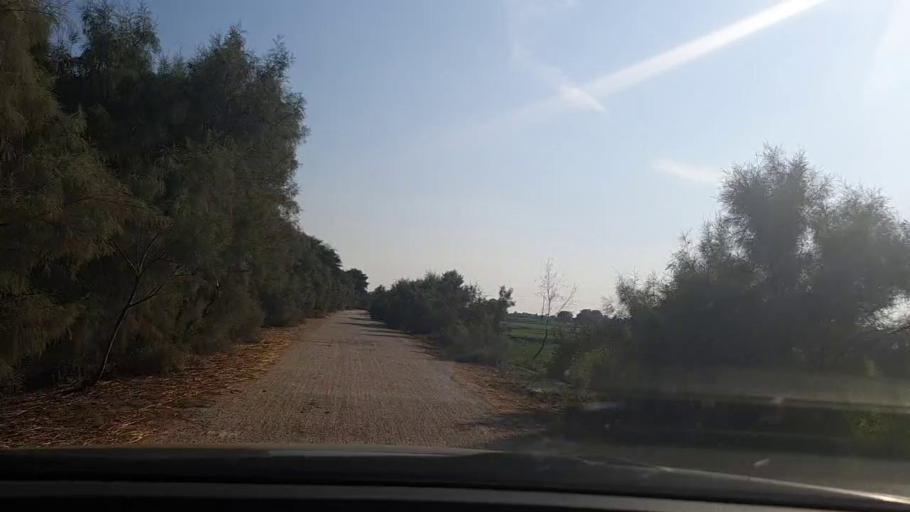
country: PK
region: Sindh
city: Sehwan
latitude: 26.3082
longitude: 68.0010
